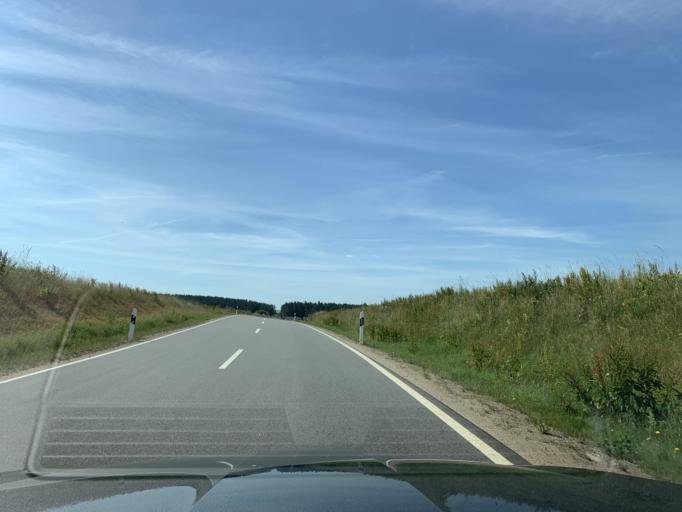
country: DE
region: Bavaria
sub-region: Upper Palatinate
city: Schwarzhofen
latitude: 49.3567
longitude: 12.3237
